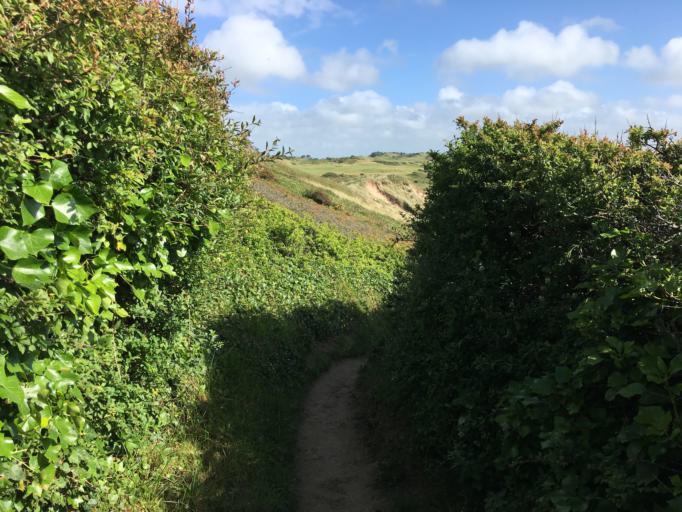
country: GB
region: England
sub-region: Cornwall
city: Polzeath
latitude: 50.5563
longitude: -4.9284
